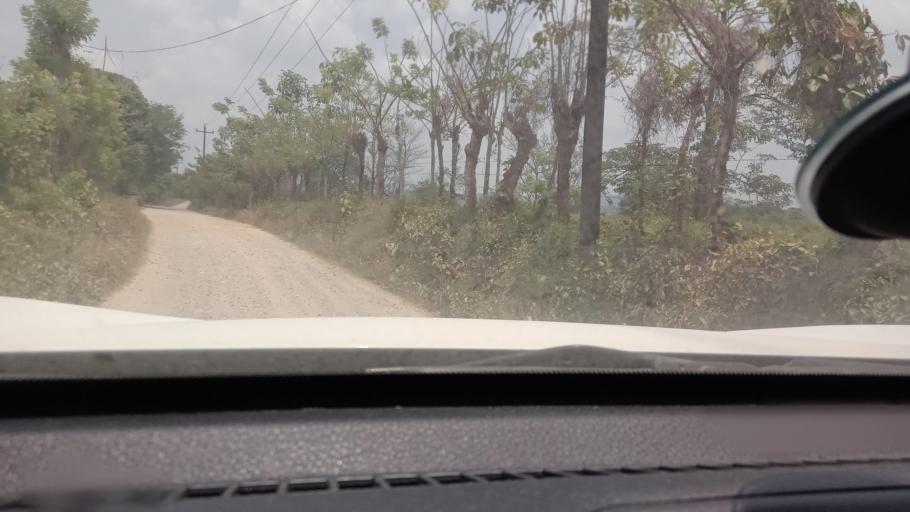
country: MX
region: Tabasco
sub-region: Huimanguillo
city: Francisco Rueda
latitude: 17.5070
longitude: -93.8996
